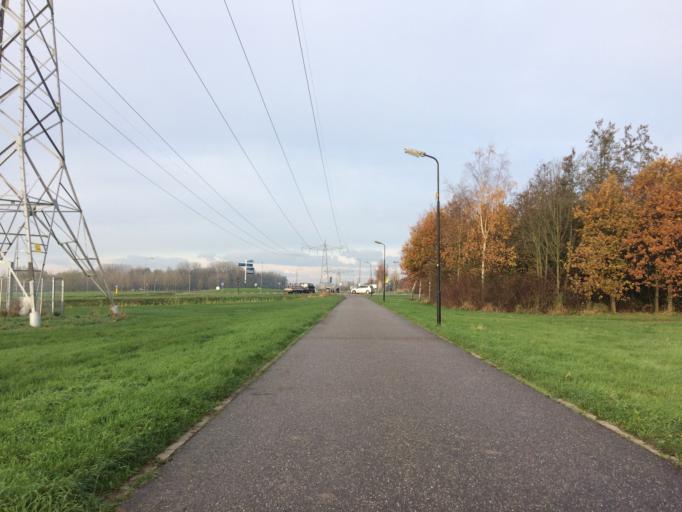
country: NL
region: Gelderland
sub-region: Gemeente Maasdriel
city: Hedel
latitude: 51.7182
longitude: 5.2587
